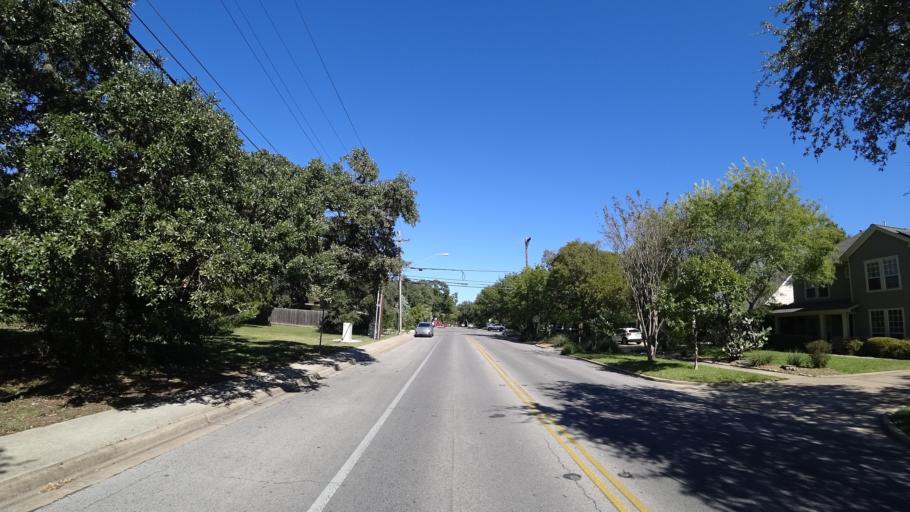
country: US
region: Texas
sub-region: Travis County
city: Austin
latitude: 30.3168
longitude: -97.7465
